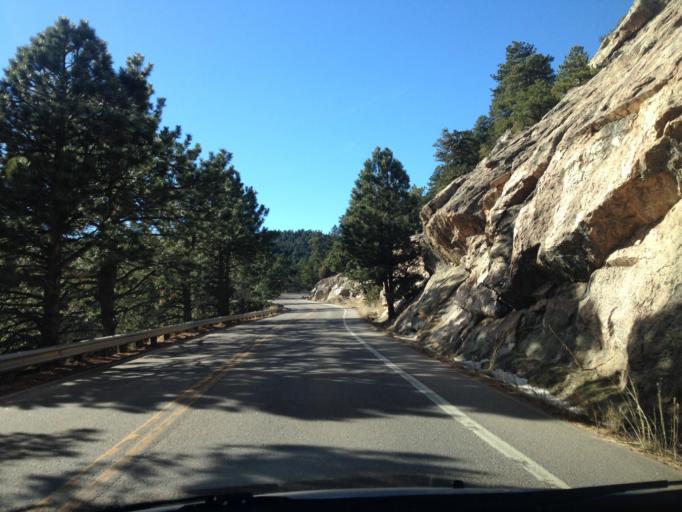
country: US
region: Colorado
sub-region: Boulder County
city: Boulder
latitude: 39.9990
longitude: -105.3056
